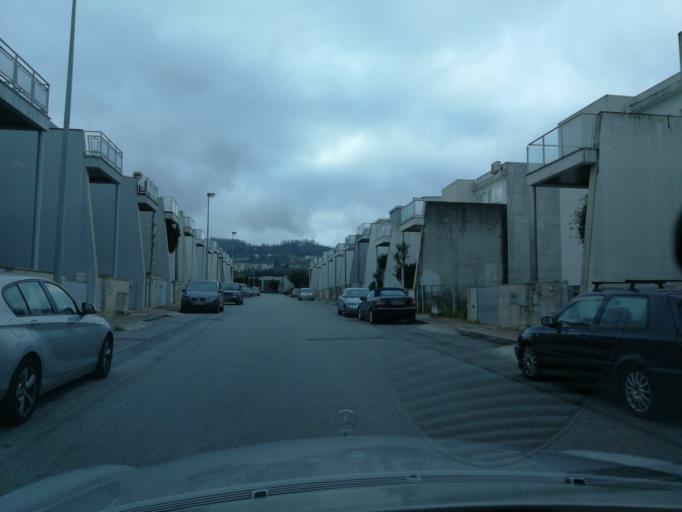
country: PT
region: Braga
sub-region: Braga
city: Braga
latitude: 41.5446
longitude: -8.3946
